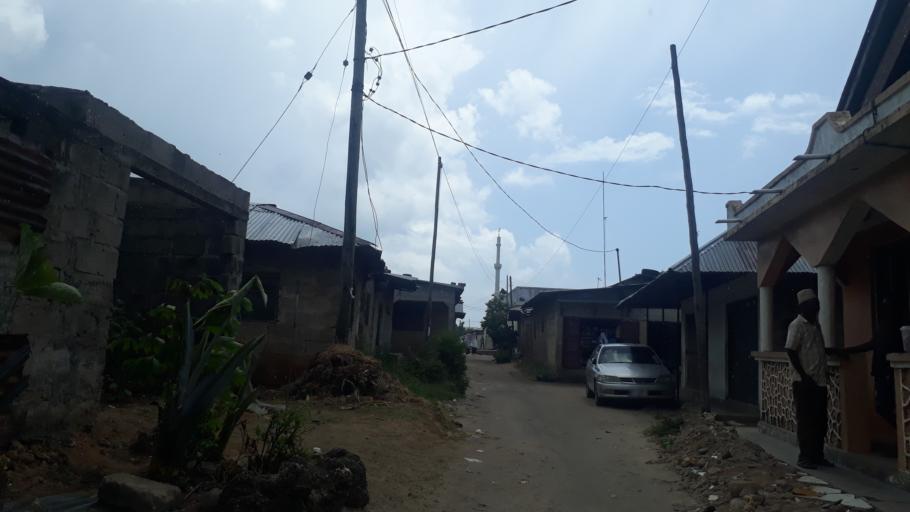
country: TZ
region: Zanzibar Urban/West
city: Zanzibar
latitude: -6.1780
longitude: 39.2098
